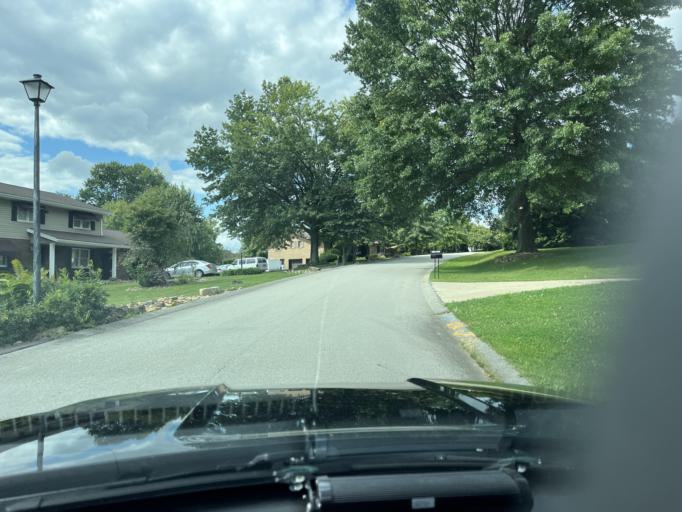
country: US
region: Pennsylvania
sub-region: Fayette County
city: South Uniontown
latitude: 39.8964
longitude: -79.7632
